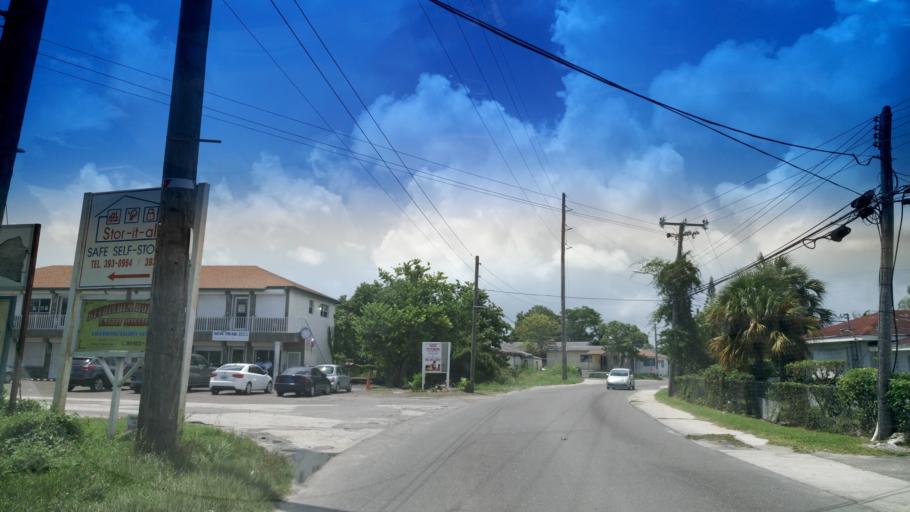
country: BS
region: New Providence
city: Nassau
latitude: 25.0418
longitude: -77.3255
